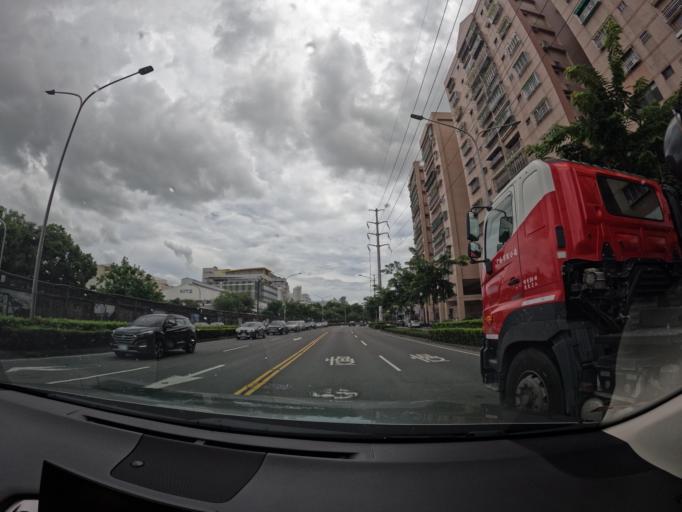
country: TW
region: Kaohsiung
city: Kaohsiung
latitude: 22.7264
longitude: 120.3098
